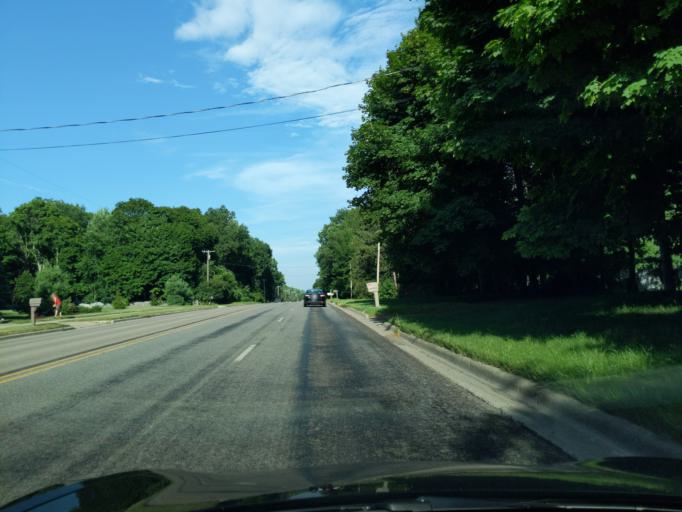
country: US
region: Michigan
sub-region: Ingham County
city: Okemos
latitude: 42.7470
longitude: -84.4408
